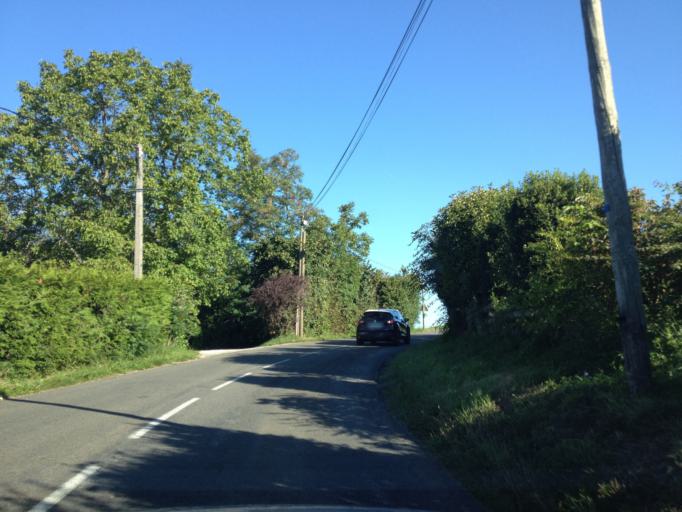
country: FR
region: Rhone-Alpes
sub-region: Departement de la Savoie
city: Mouxy
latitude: 45.7040
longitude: 5.9507
